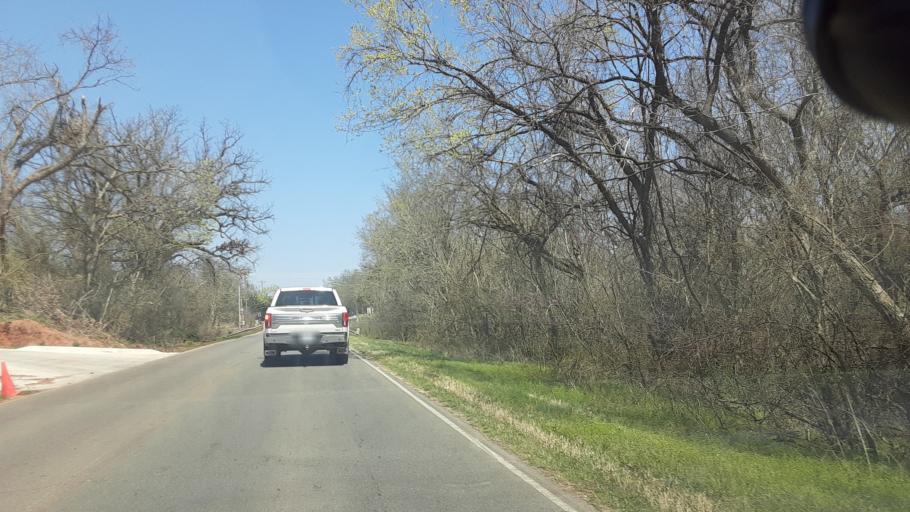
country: US
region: Oklahoma
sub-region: Oklahoma County
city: Edmond
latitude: 35.7387
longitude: -97.4785
